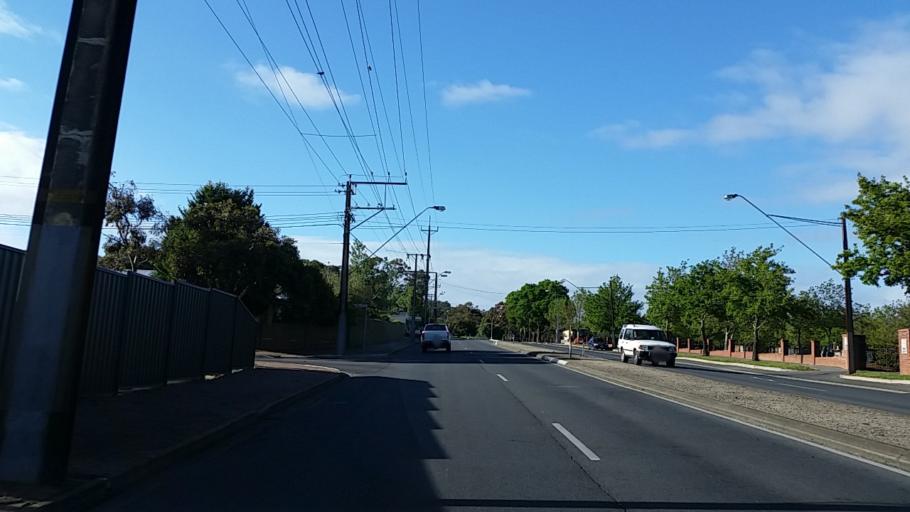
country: AU
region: South Australia
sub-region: Mitcham
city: Clapham
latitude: -34.9970
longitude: 138.5931
